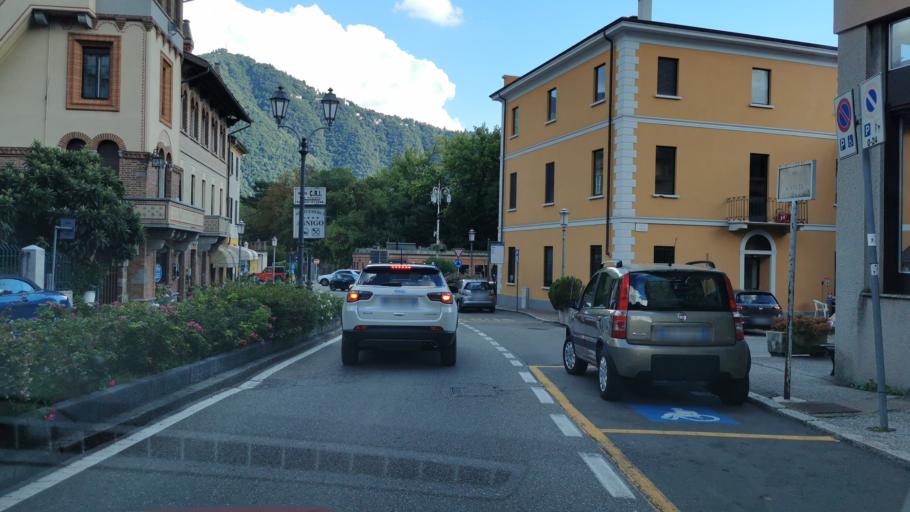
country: IT
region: Lombardy
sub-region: Provincia di Como
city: Cernobbio
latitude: 45.8408
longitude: 9.0747
